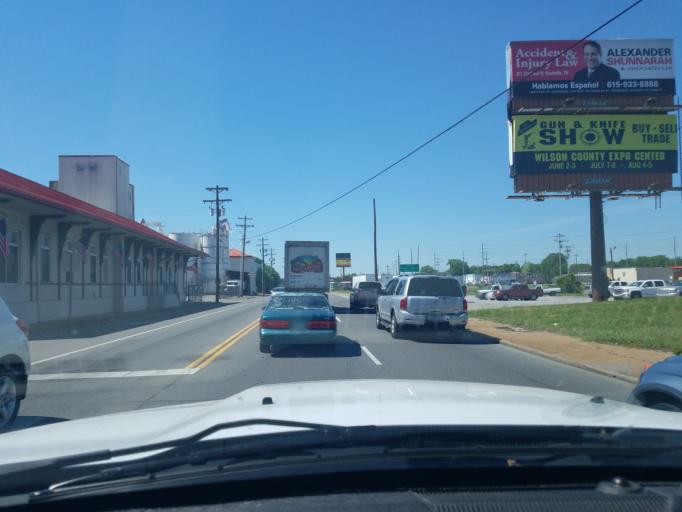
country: US
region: Tennessee
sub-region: Wilson County
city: Lebanon
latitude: 36.2069
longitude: -86.2913
